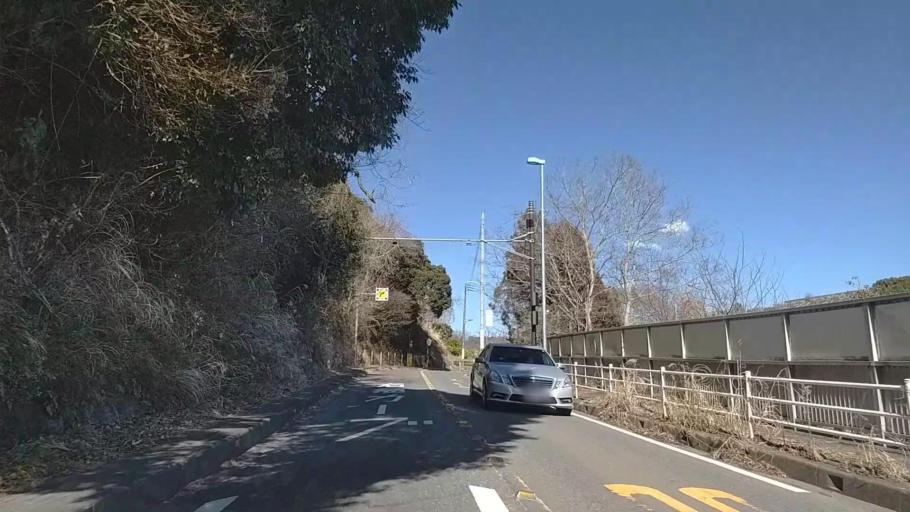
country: JP
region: Kanagawa
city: Zushi
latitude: 35.3250
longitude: 139.5817
